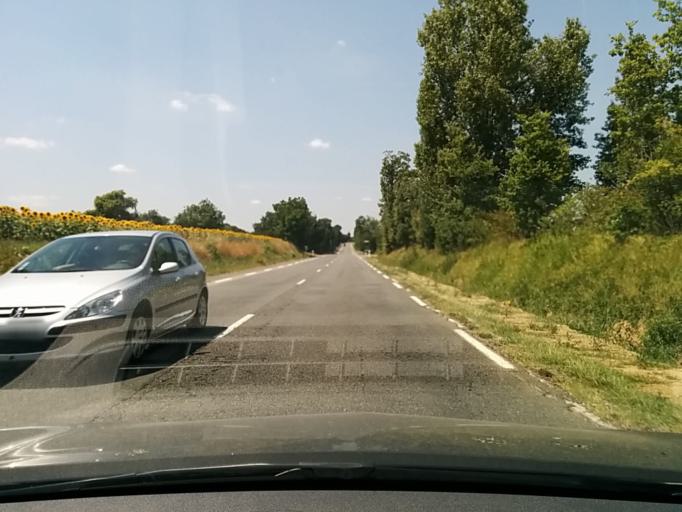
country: FR
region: Midi-Pyrenees
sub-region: Departement du Gers
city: Pujaudran
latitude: 43.6026
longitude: 1.0198
